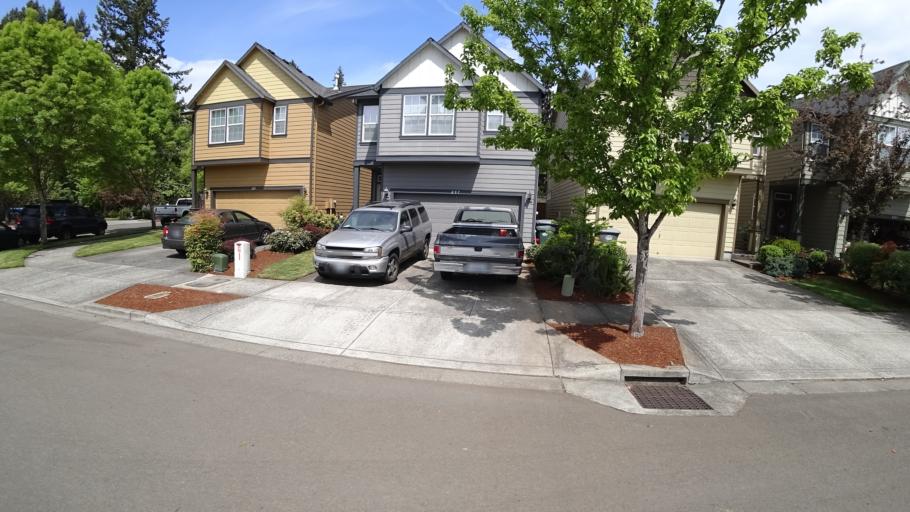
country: US
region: Oregon
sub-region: Washington County
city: Hillsboro
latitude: 45.5402
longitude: -122.9981
